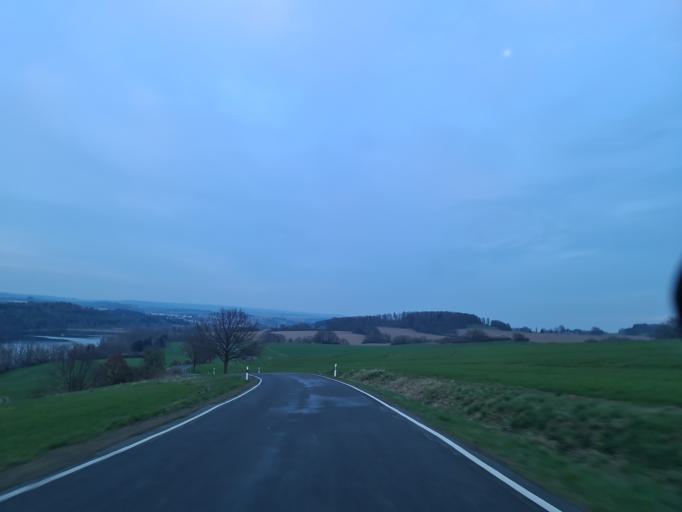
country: DE
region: Saxony
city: Bosenbrunn
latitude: 50.4191
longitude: 12.1184
